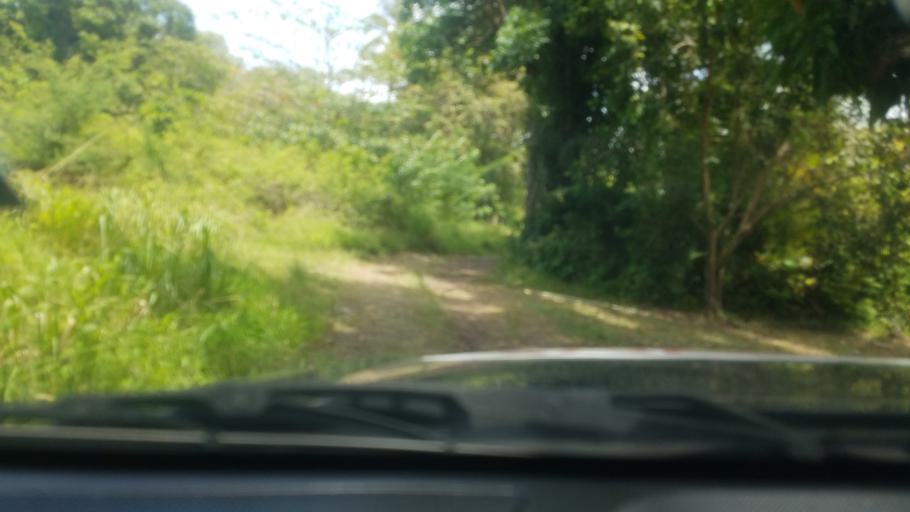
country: LC
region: Laborie Quarter
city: Laborie
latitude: 13.7712
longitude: -60.9404
